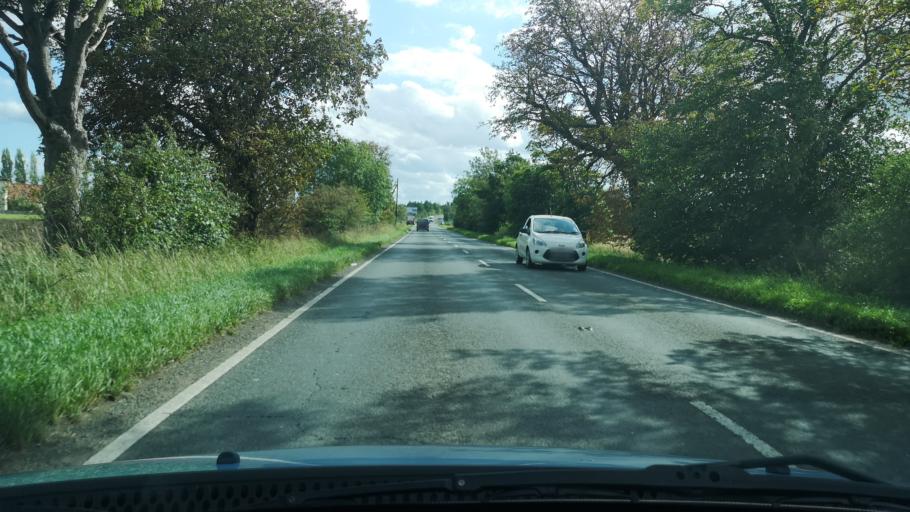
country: GB
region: England
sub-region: North Lincolnshire
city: Belton
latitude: 53.5750
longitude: -0.8177
